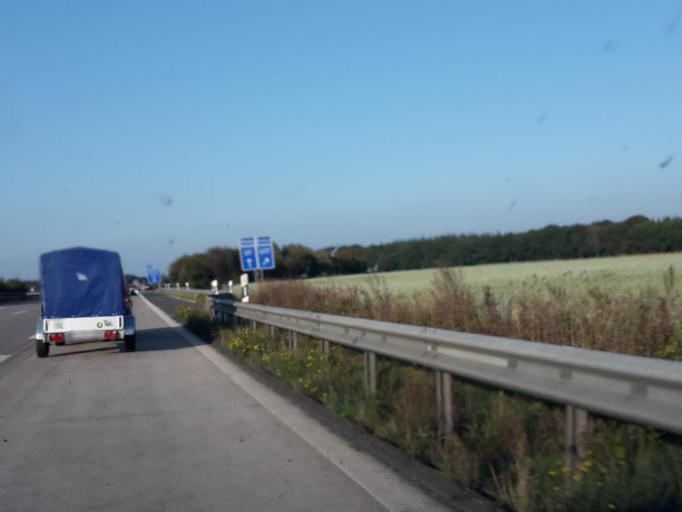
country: DE
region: Lower Saxony
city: Buehren
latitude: 52.8453
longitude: 8.2224
